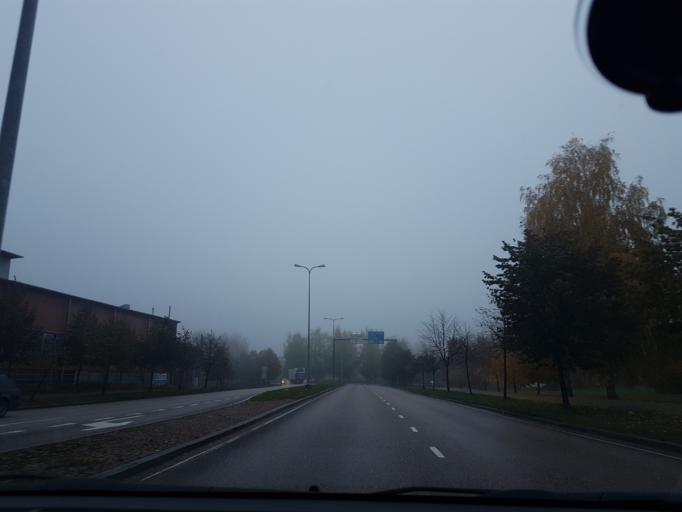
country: FI
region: Uusimaa
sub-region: Helsinki
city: Tuusula
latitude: 60.4018
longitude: 25.0303
